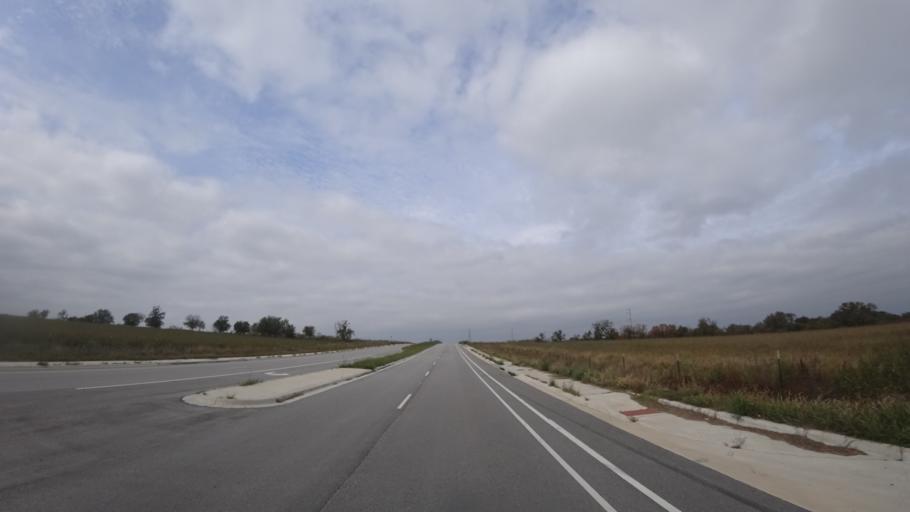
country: US
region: Texas
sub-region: Travis County
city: Manor
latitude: 30.3724
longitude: -97.5919
